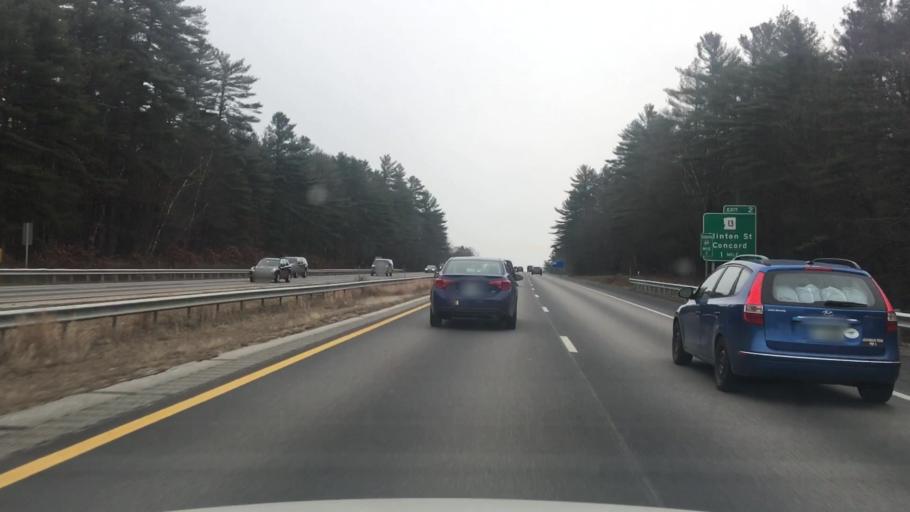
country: US
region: New Hampshire
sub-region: Merrimack County
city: Concord
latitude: 43.1843
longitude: -71.5838
